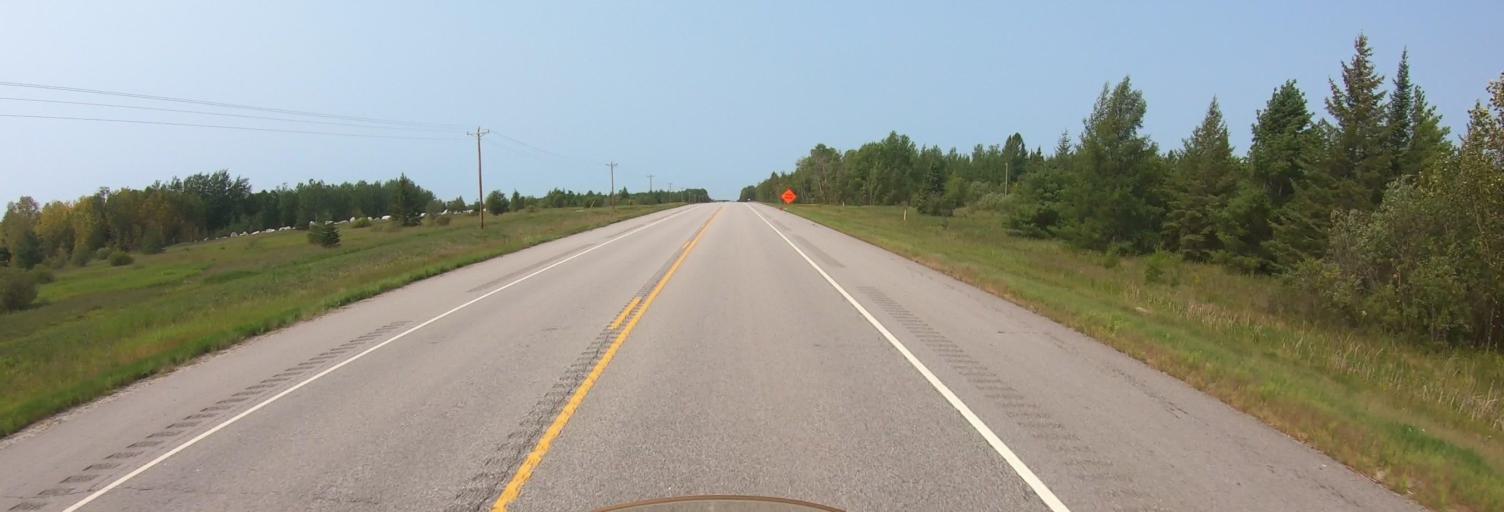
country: CA
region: Ontario
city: Fort Frances
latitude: 48.4102
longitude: -93.1565
